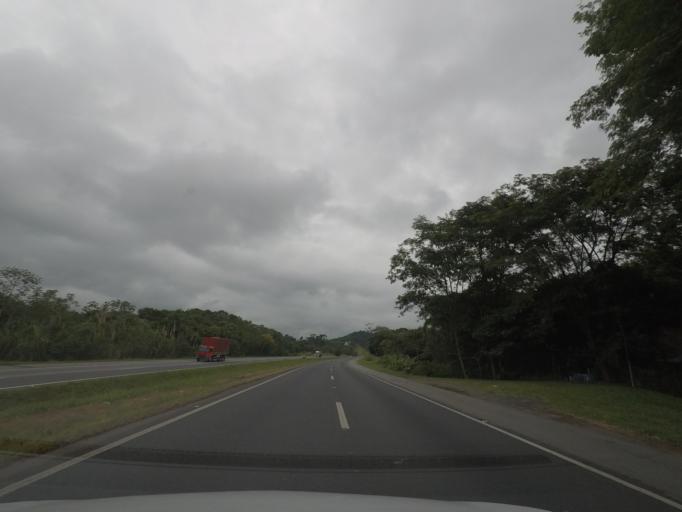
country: BR
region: Sao Paulo
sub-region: Juquia
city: Juquia
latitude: -24.3691
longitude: -47.6973
